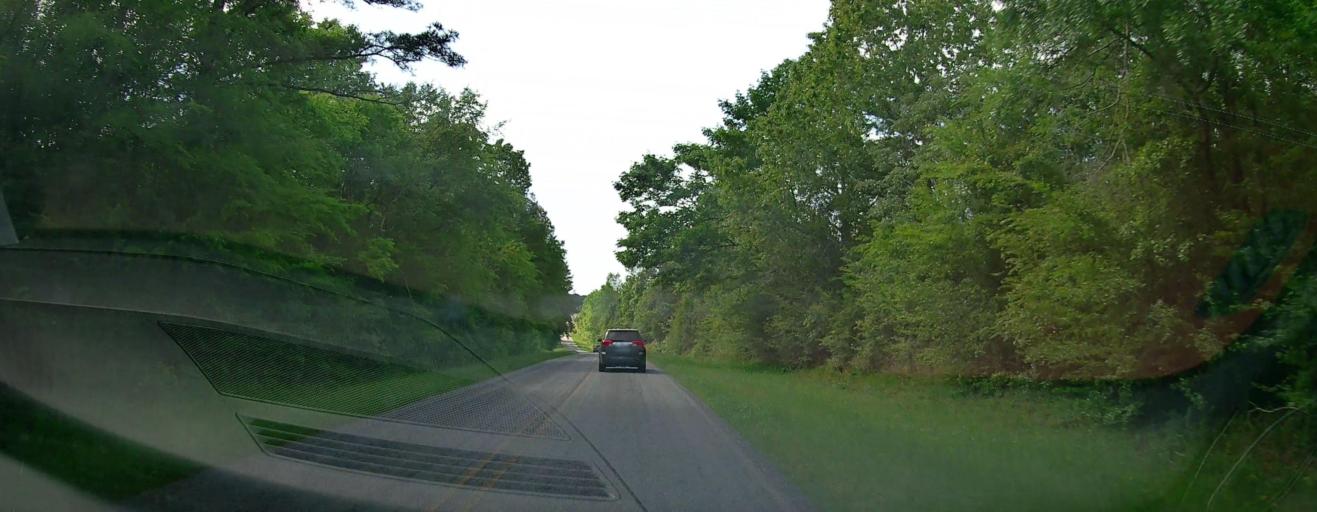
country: US
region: Georgia
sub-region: Laurens County
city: East Dublin
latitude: 32.6922
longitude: -82.9018
